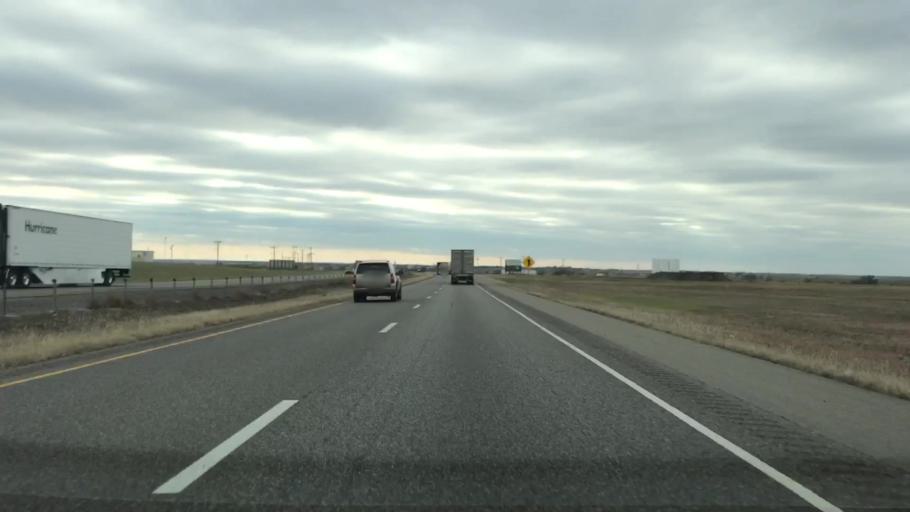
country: US
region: Oklahoma
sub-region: Beckham County
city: Sayre
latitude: 35.3375
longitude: -99.5943
